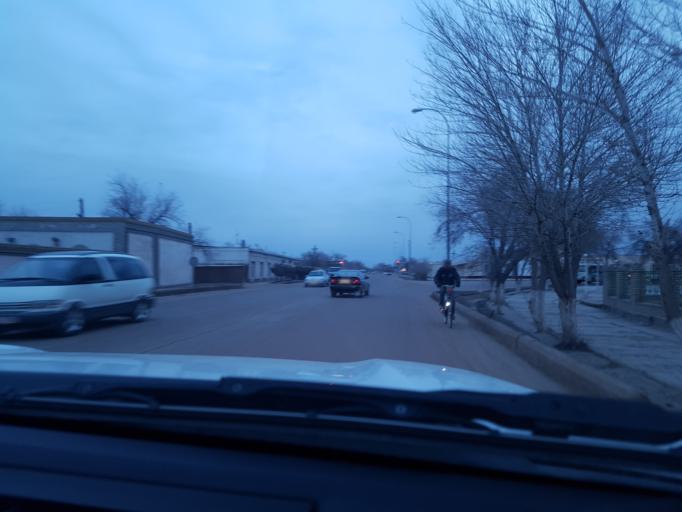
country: TM
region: Dasoguz
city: Yylanly
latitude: 41.8793
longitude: 59.6296
